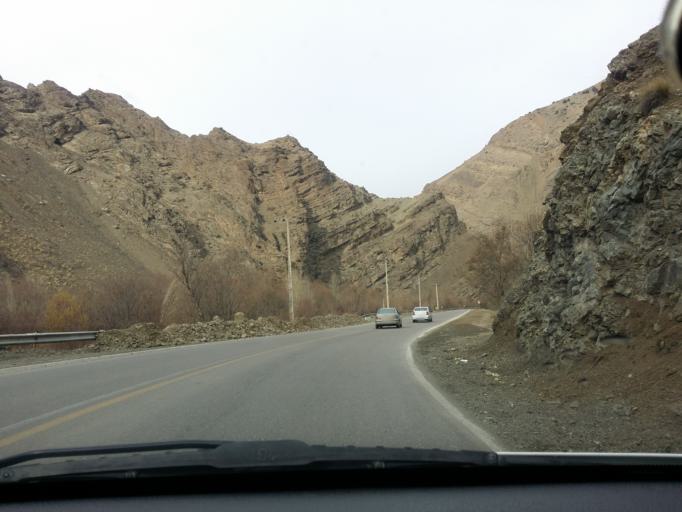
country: IR
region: Tehran
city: Tajrish
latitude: 36.0153
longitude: 51.2816
